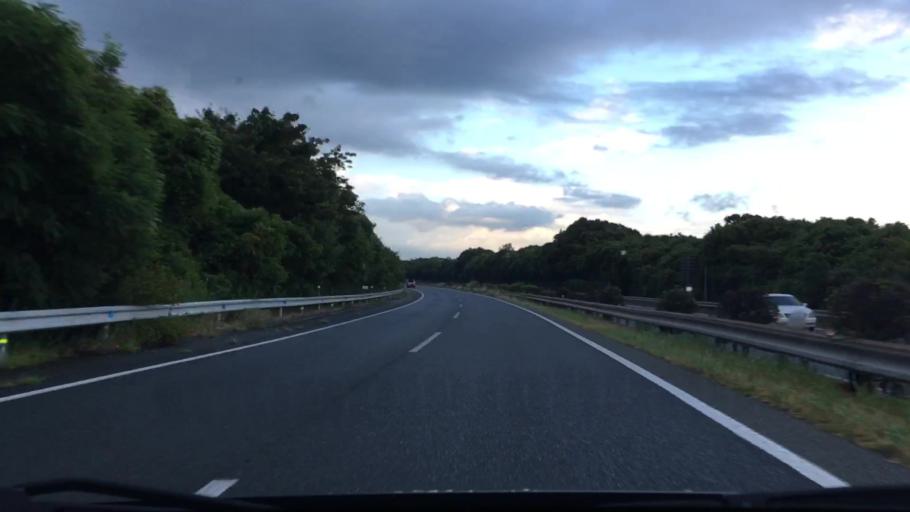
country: JP
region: Yamaguchi
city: Shimonoseki
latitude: 33.8751
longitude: 130.9680
